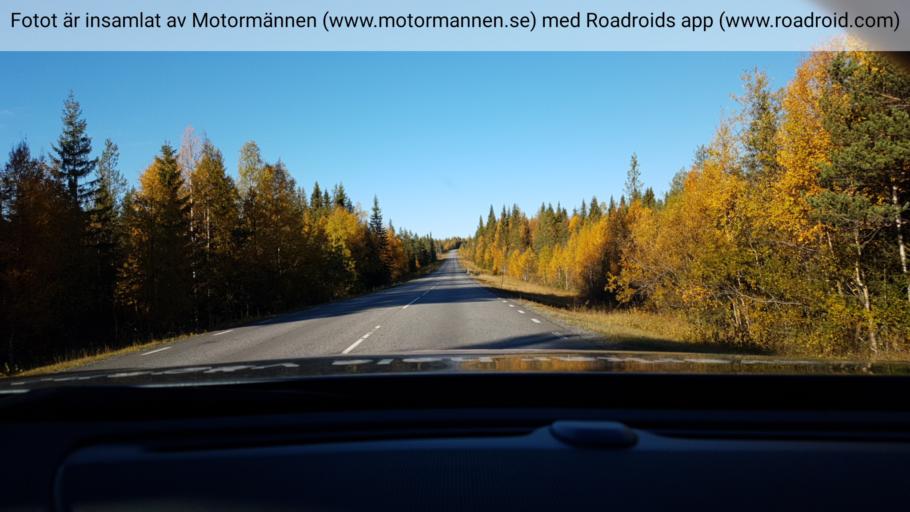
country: SE
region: Vaesterbotten
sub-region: Skelleftea Kommun
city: Storvik
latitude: 65.3371
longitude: 20.5563
